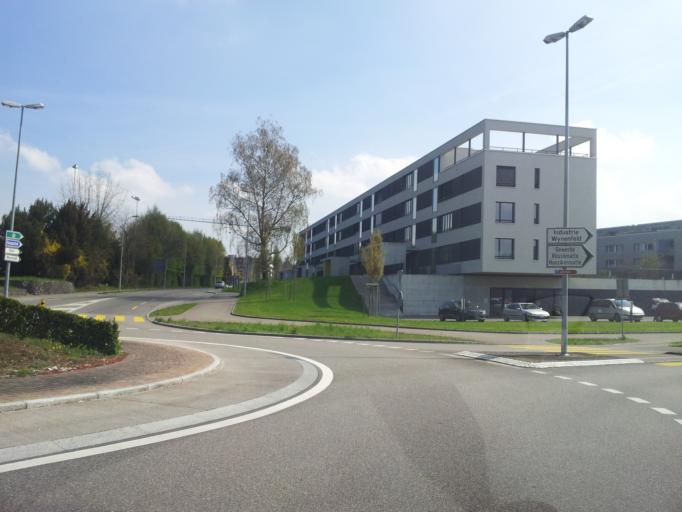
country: CH
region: Aargau
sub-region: Bezirk Aarau
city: Buchs
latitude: 47.3910
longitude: 8.0798
